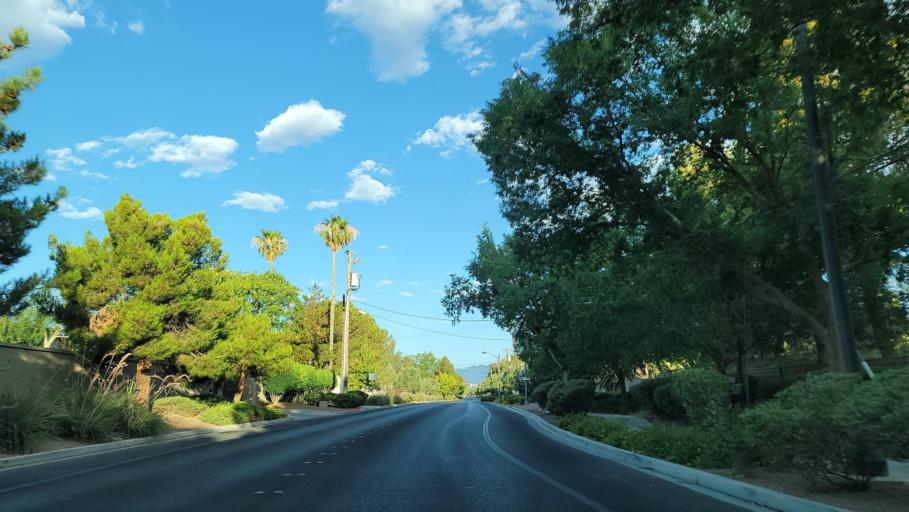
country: US
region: Nevada
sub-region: Clark County
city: Las Vegas
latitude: 36.1662
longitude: -115.1753
